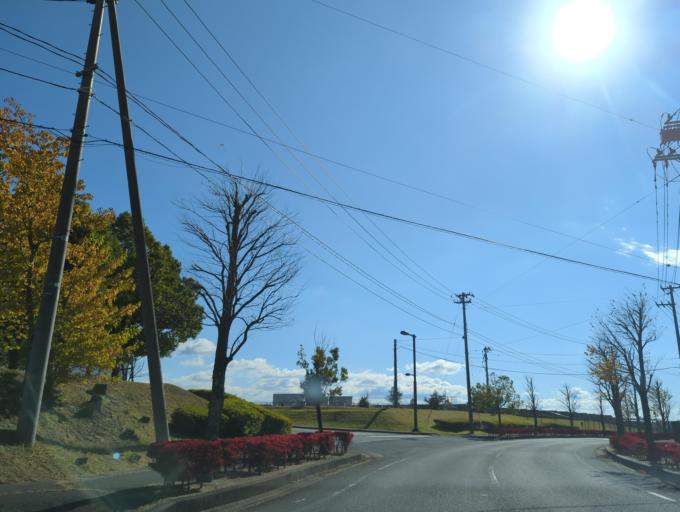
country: JP
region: Fukushima
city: Koriyama
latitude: 37.4489
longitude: 140.3151
